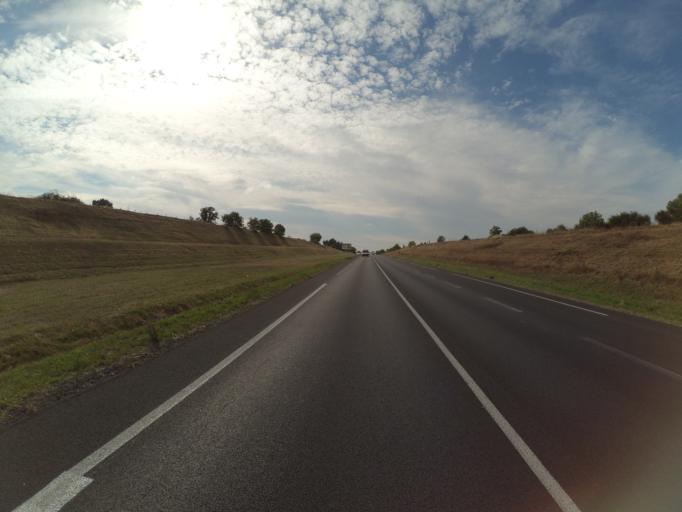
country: FR
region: Pays de la Loire
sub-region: Departement de Maine-et-Loire
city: Distre
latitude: 47.2488
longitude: -0.1038
